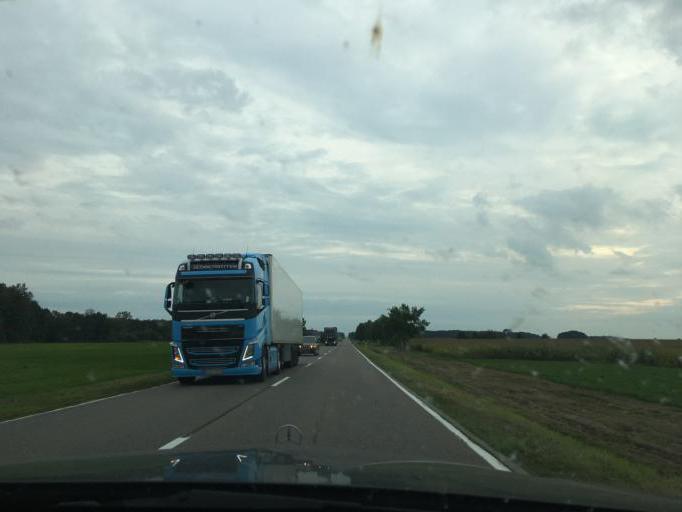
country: PL
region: Podlasie
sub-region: Powiat lomzynski
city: Sniadowo
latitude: 52.9798
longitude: 21.9002
